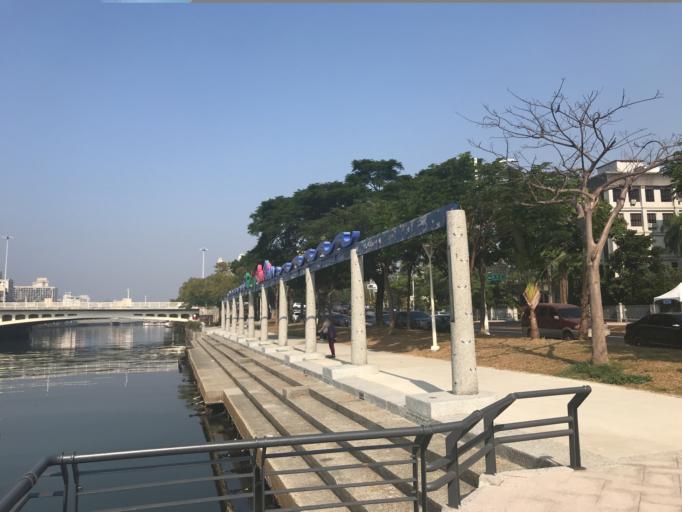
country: TW
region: Kaohsiung
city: Kaohsiung
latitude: 22.6257
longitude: 120.2893
